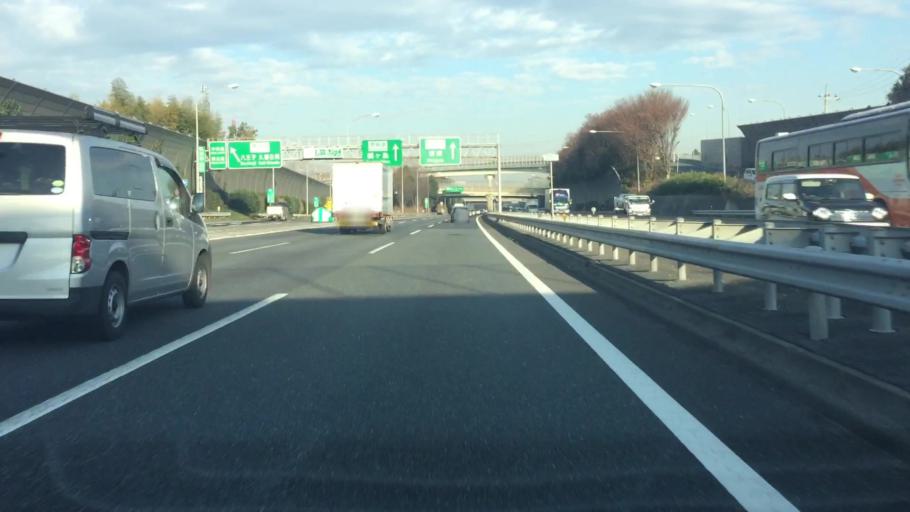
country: JP
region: Saitama
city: Sakado
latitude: 35.9293
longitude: 139.4087
